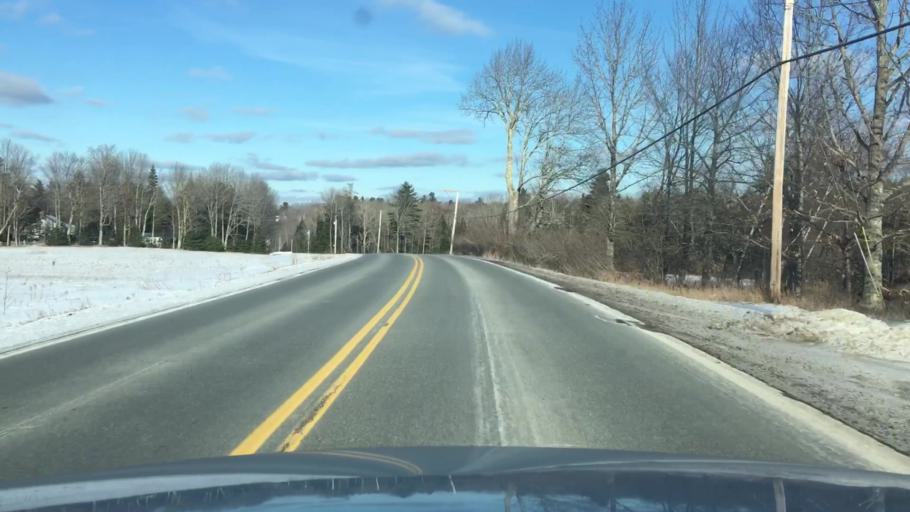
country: US
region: Maine
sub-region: Penobscot County
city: Holden
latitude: 44.7571
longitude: -68.5966
